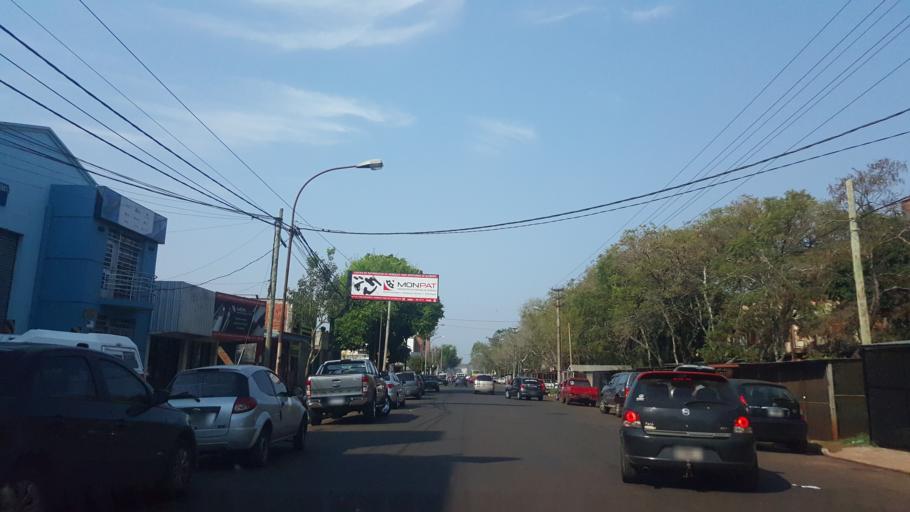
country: AR
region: Misiones
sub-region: Departamento de Capital
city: Posadas
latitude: -27.3951
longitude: -55.9052
